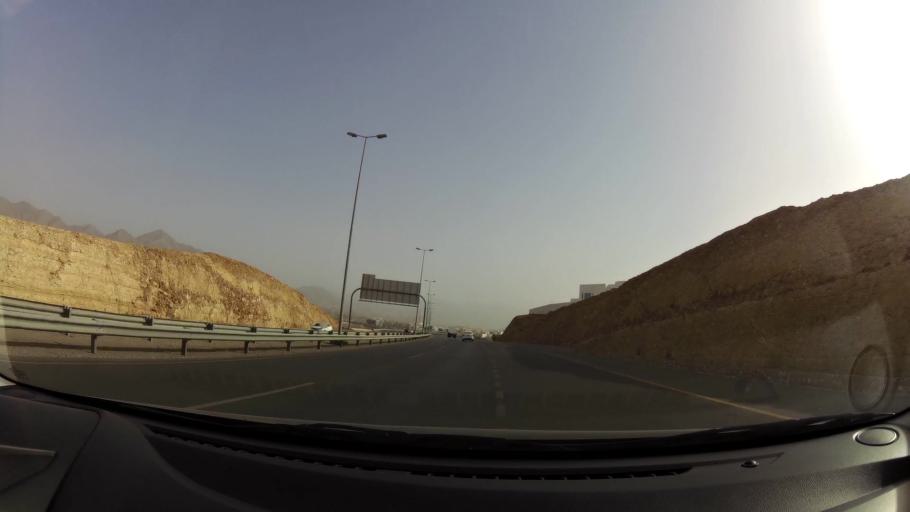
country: OM
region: Muhafazat Masqat
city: Bawshar
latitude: 23.5554
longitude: 58.3683
